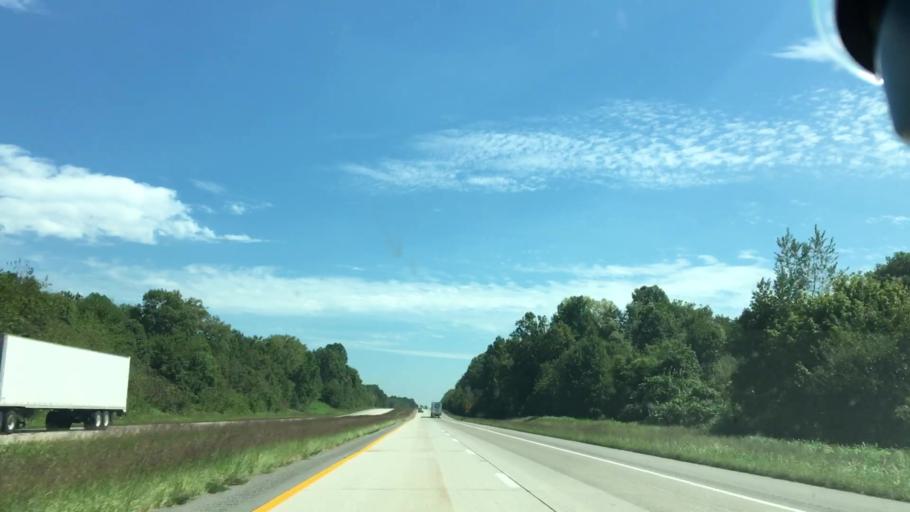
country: US
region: Kentucky
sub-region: Henderson County
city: Henderson
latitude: 37.7800
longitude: -87.4539
